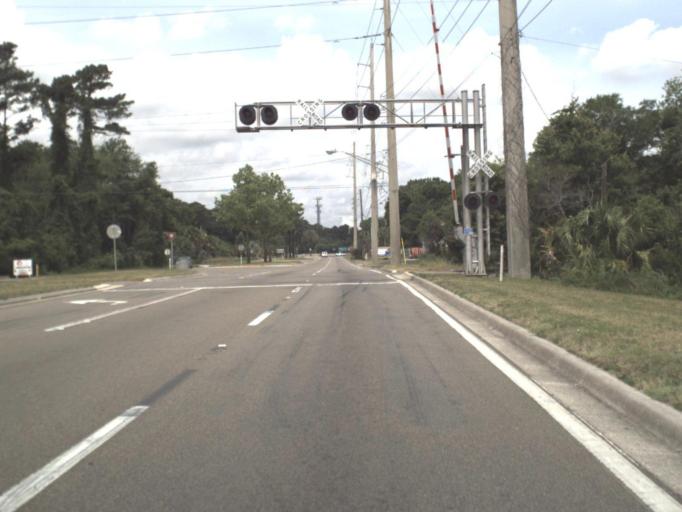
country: US
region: Florida
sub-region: Duval County
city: Jacksonville
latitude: 30.4074
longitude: -81.6384
